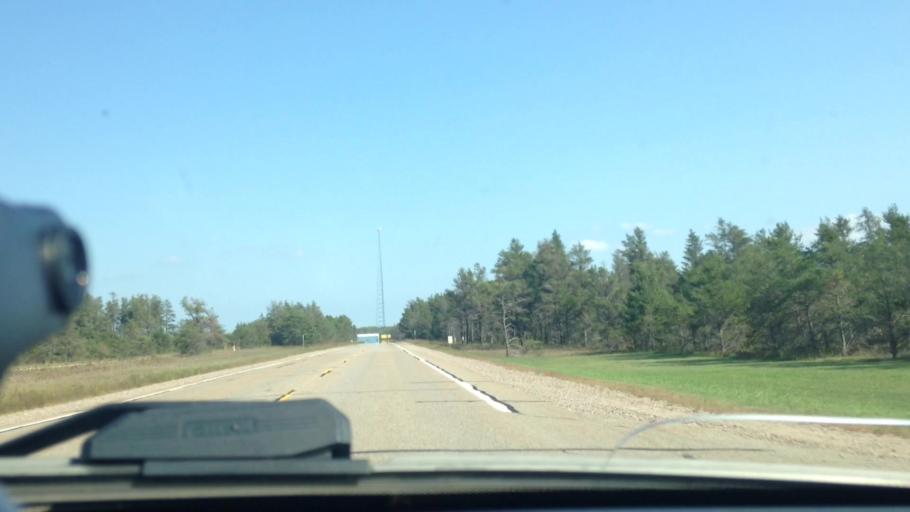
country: US
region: Michigan
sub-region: Chippewa County
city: Sault Ste. Marie
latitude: 46.3589
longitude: -84.8044
